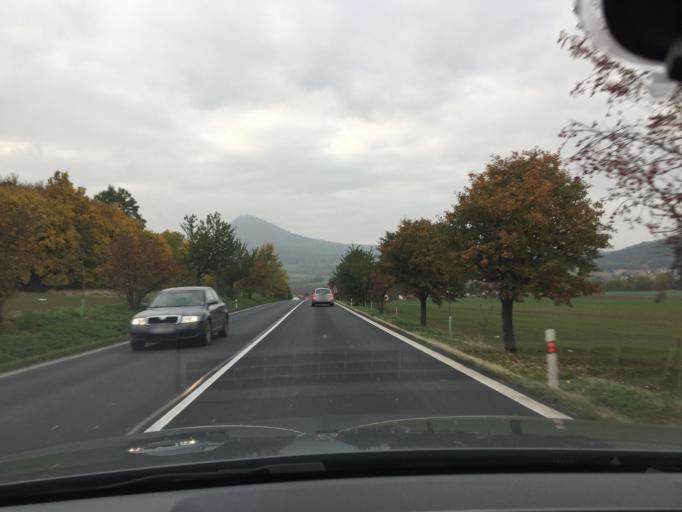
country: CZ
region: Ustecky
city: Velemin
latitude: 50.5345
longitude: 13.9835
